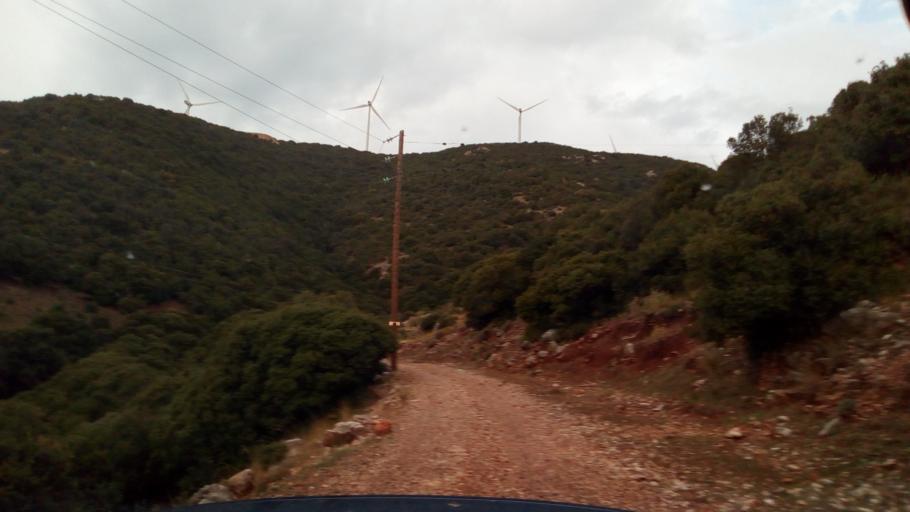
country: GR
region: West Greece
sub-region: Nomos Achaias
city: Kamarai
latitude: 38.4148
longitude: 22.0500
